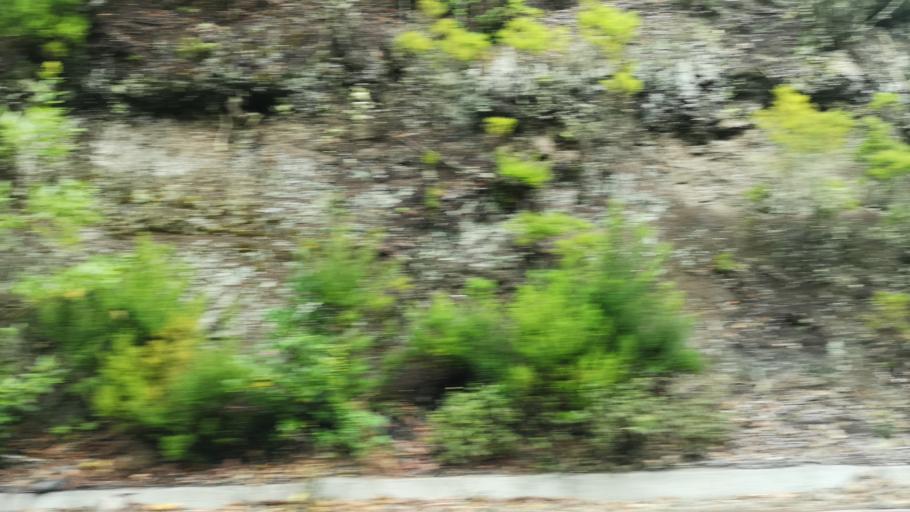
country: ES
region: Canary Islands
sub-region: Provincia de Santa Cruz de Tenerife
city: Vallehermosa
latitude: 28.1458
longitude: -17.2887
